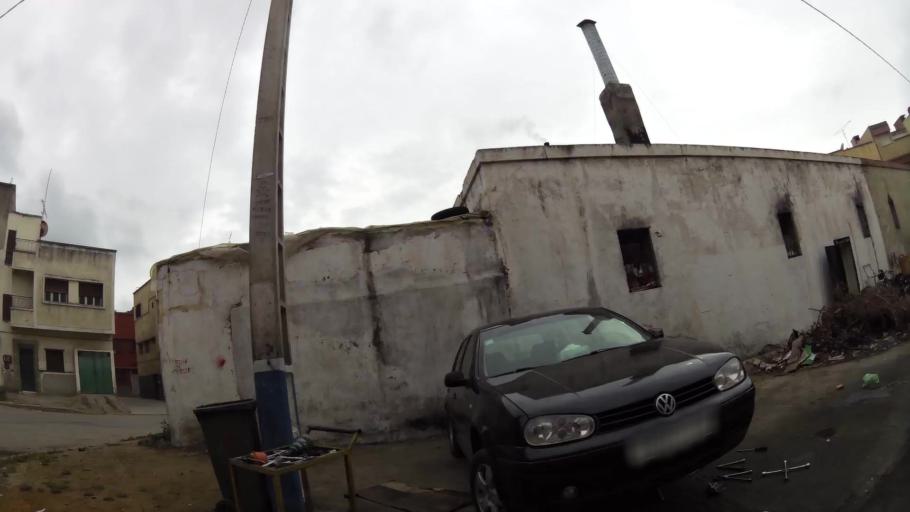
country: MA
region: Rabat-Sale-Zemmour-Zaer
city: Sale
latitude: 34.0478
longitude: -6.7959
